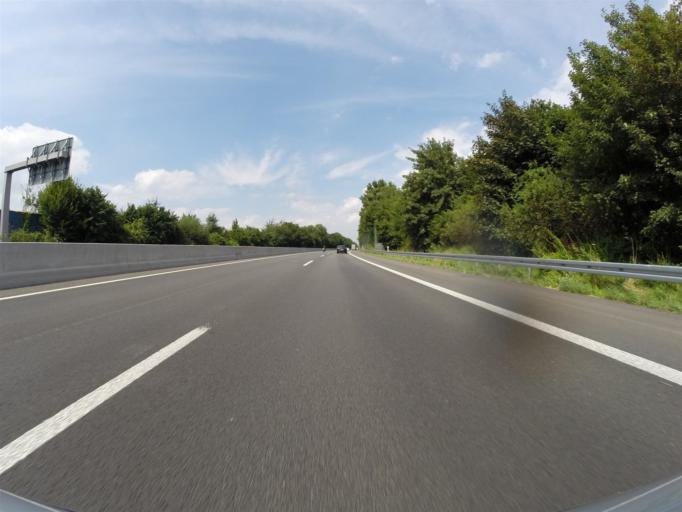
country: DE
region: North Rhine-Westphalia
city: Buende
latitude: 52.1885
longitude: 8.5798
